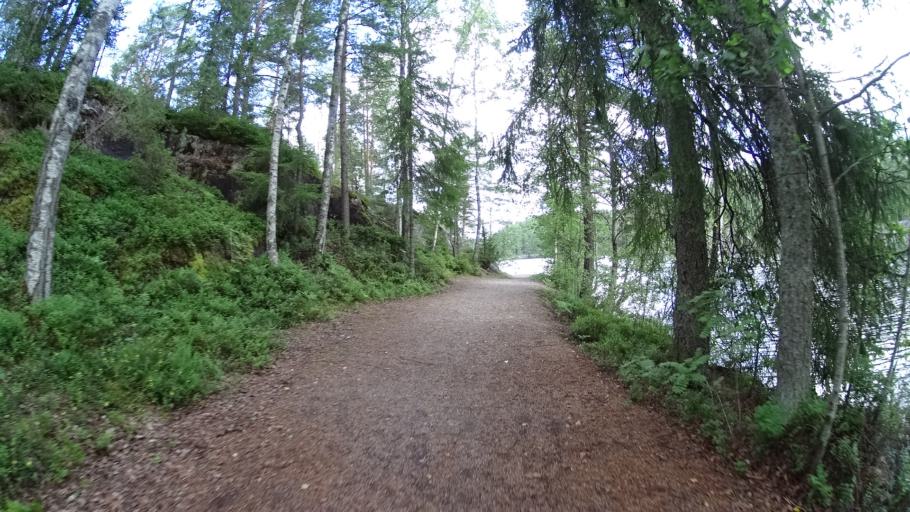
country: FI
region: Uusimaa
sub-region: Helsinki
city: Espoo
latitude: 60.3208
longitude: 24.6621
